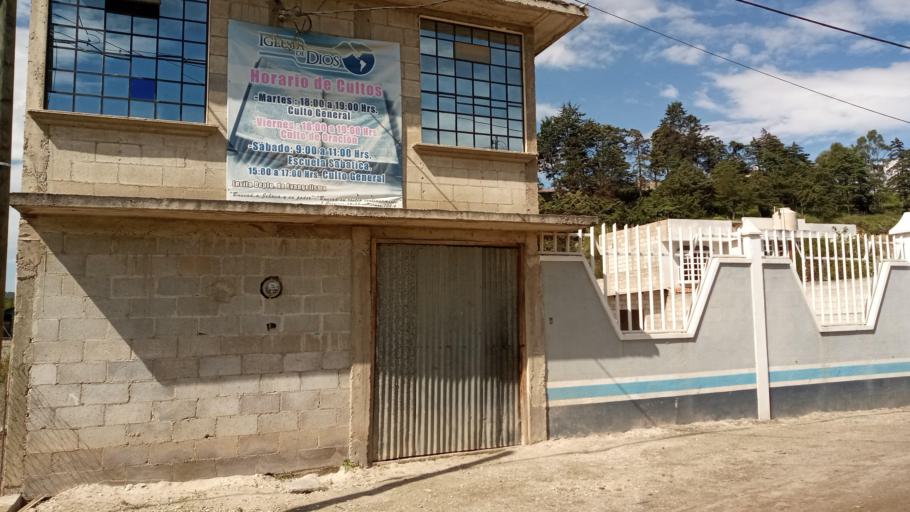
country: GT
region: Quetzaltenango
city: Quetzaltenango
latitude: 14.8459
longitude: -91.5096
